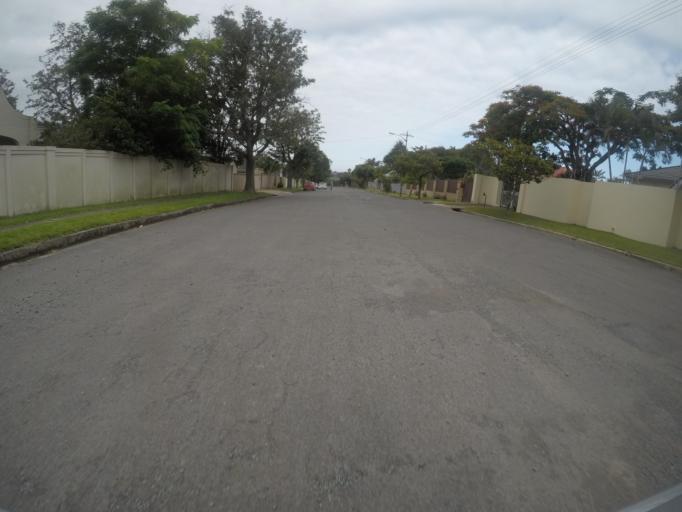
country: ZA
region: Eastern Cape
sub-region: Buffalo City Metropolitan Municipality
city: East London
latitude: -32.9904
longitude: 27.8956
